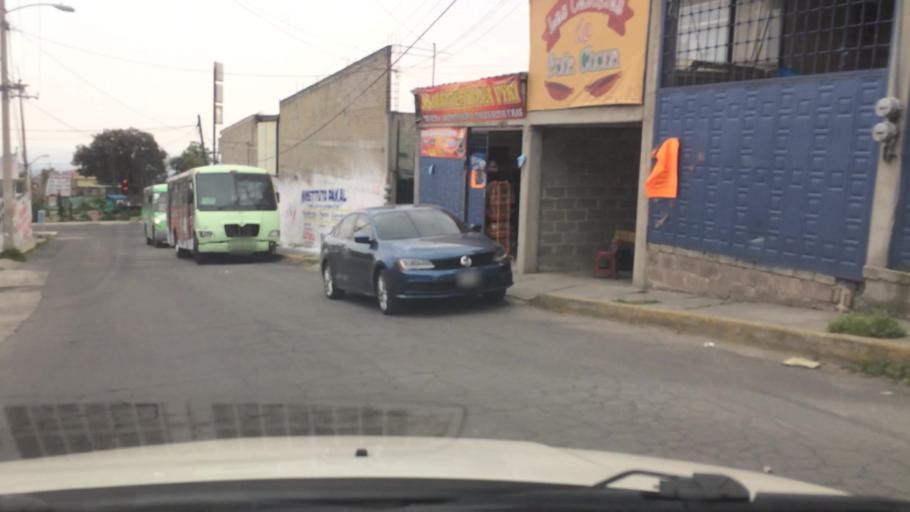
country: MX
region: Mexico City
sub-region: Tlalpan
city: Lomas de Tepemecatl
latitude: 19.2669
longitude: -99.2052
